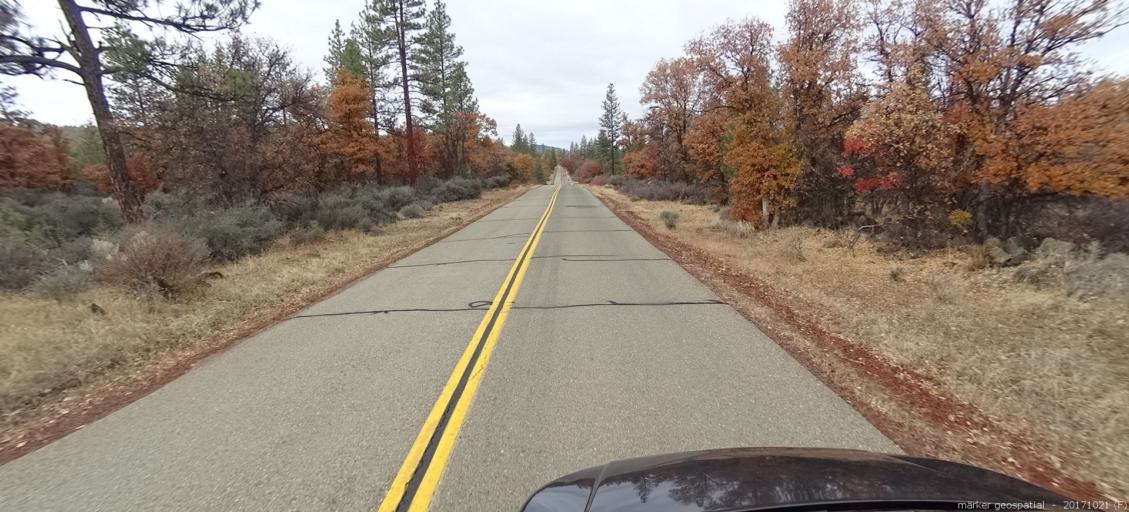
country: US
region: California
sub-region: Shasta County
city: Burney
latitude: 40.9317
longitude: -121.5579
